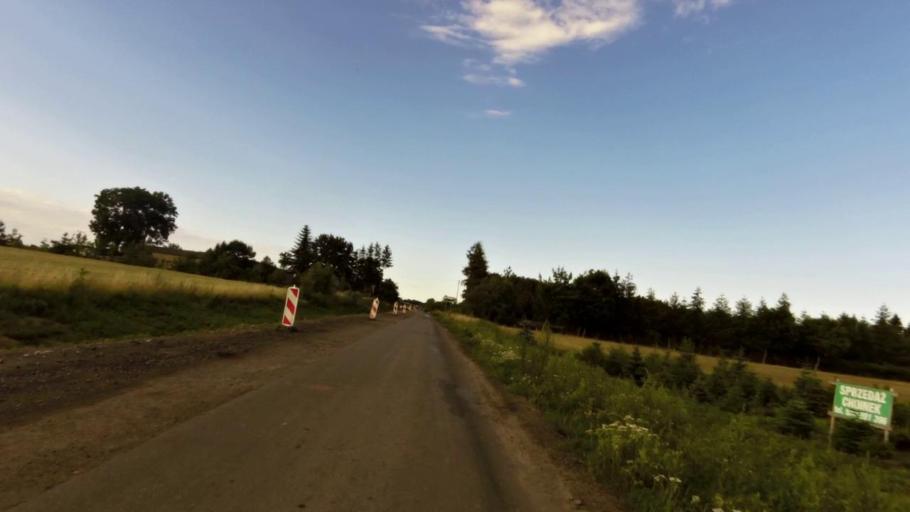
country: PL
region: West Pomeranian Voivodeship
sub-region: Powiat slawienski
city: Darlowo
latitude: 54.4095
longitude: 16.3930
